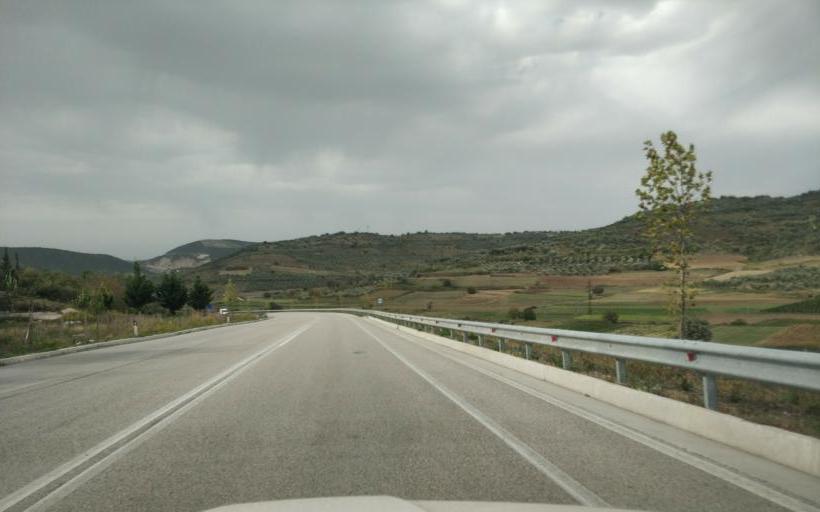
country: AL
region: Fier
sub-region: Rrethi i Mallakastres
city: Fratar
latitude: 40.4937
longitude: 19.8299
